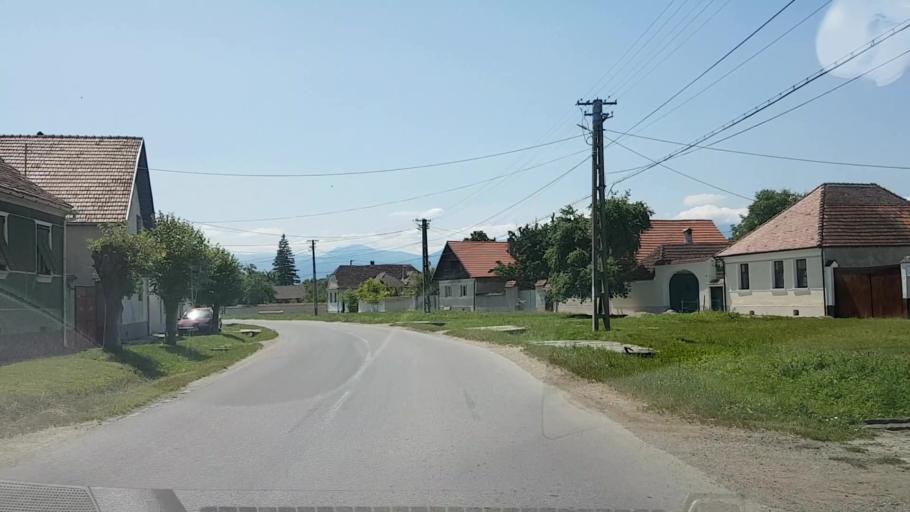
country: RO
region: Brasov
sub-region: Comuna Voila
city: Voila
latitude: 45.8388
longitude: 24.8326
